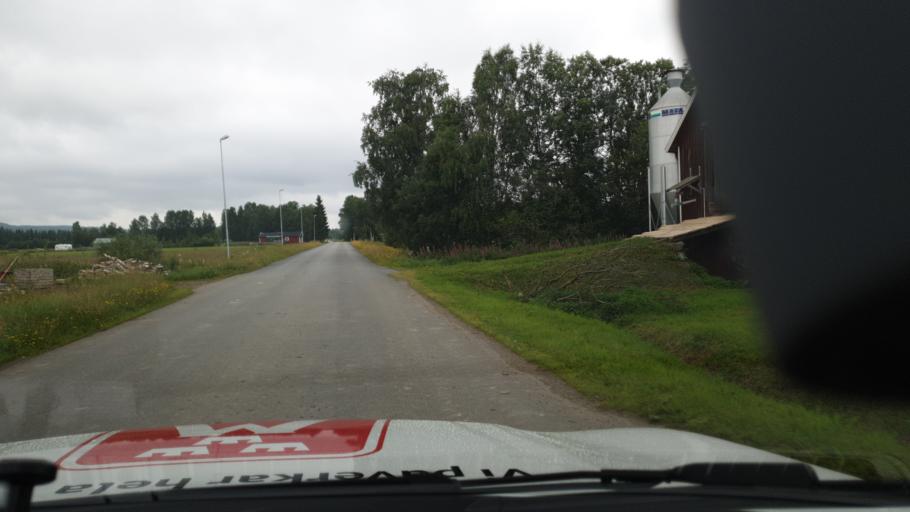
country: SE
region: Vaesterbotten
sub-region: Vannas Kommun
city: Vannasby
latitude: 63.9525
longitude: 19.8682
